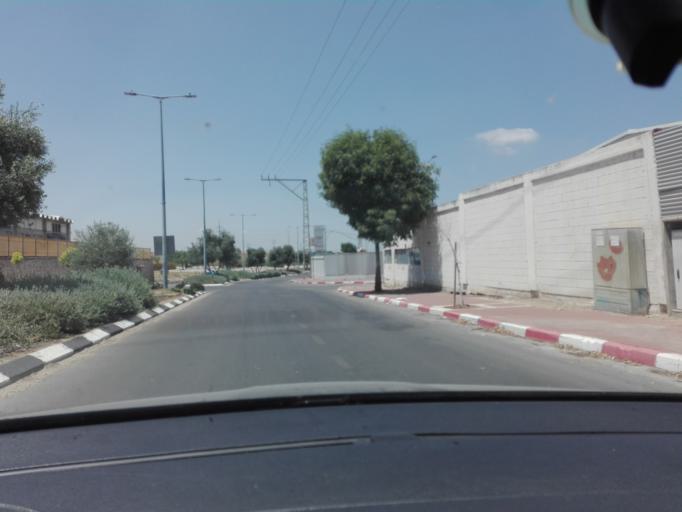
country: IL
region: Southern District
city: Qiryat Gat
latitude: 31.5945
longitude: 34.7788
